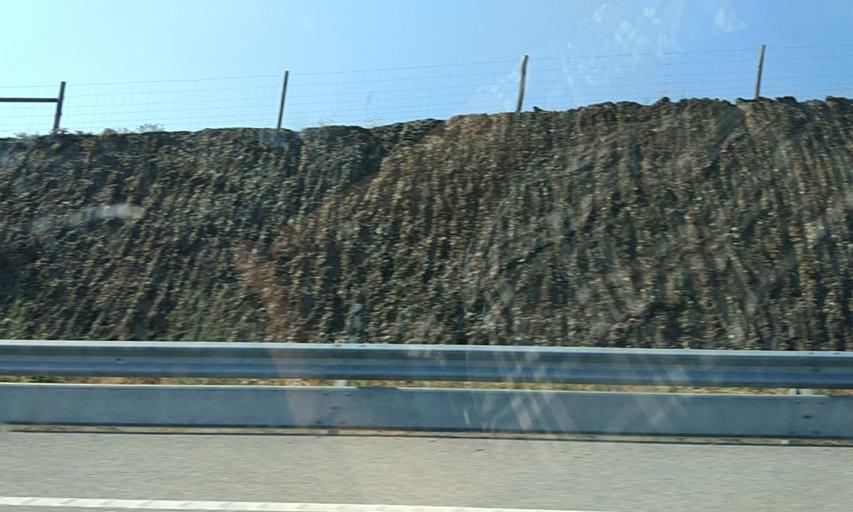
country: PT
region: Braganca
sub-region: Mirandela
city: Mirandela
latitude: 41.5192
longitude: -7.1461
